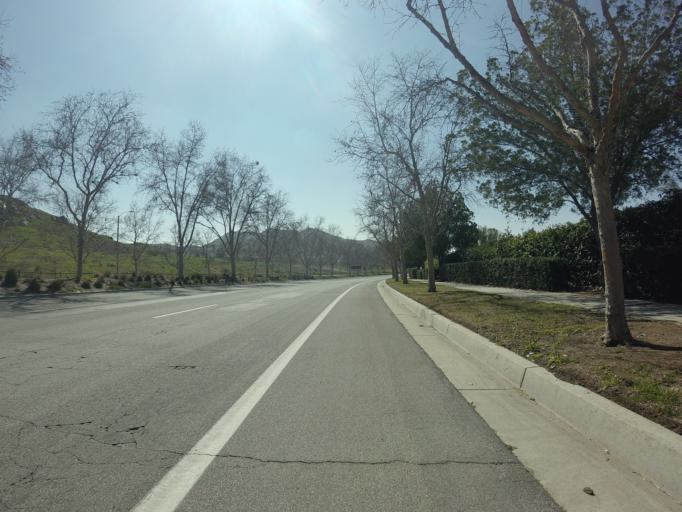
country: US
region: California
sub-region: Riverside County
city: Moreno Valley
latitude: 33.8968
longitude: -117.1760
